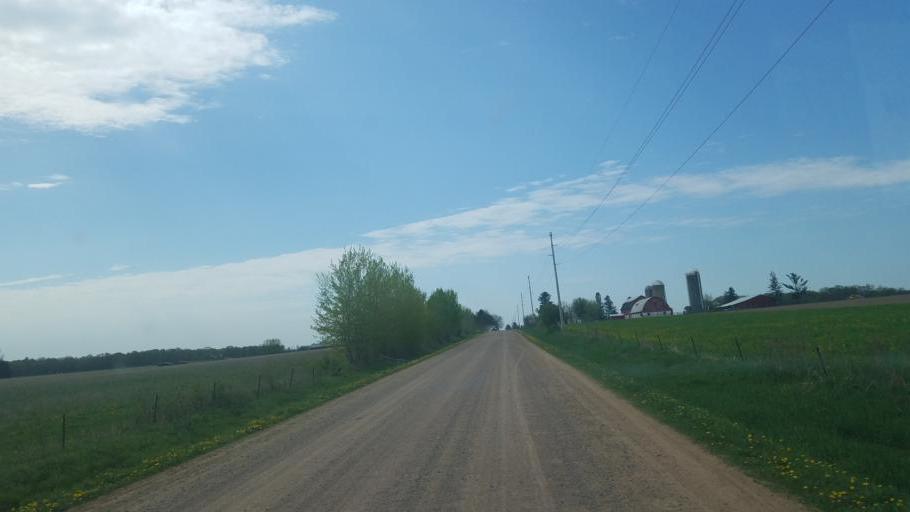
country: US
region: Wisconsin
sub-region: Marathon County
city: Spencer
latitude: 44.6310
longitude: -90.3767
